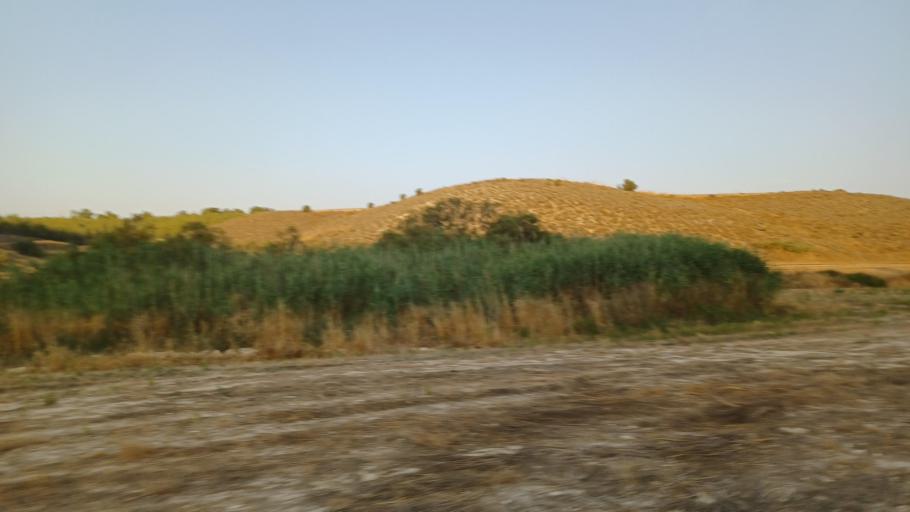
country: CY
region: Lefkosia
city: Lympia
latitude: 34.9960
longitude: 33.5212
